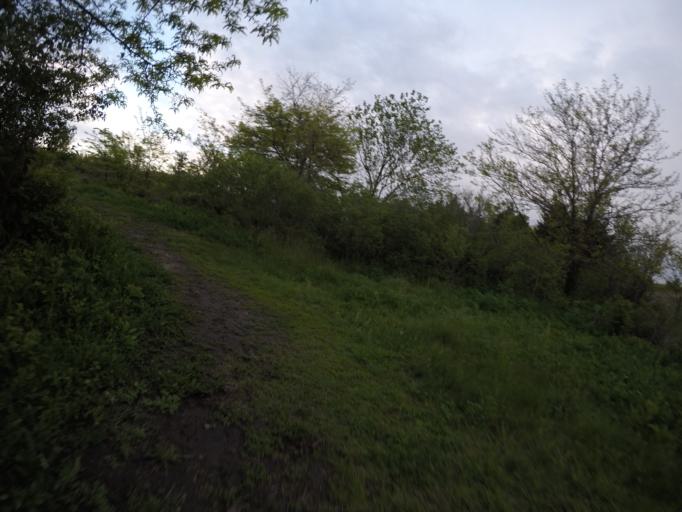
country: US
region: Kansas
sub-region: Riley County
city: Manhattan
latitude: 39.2213
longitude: -96.6238
